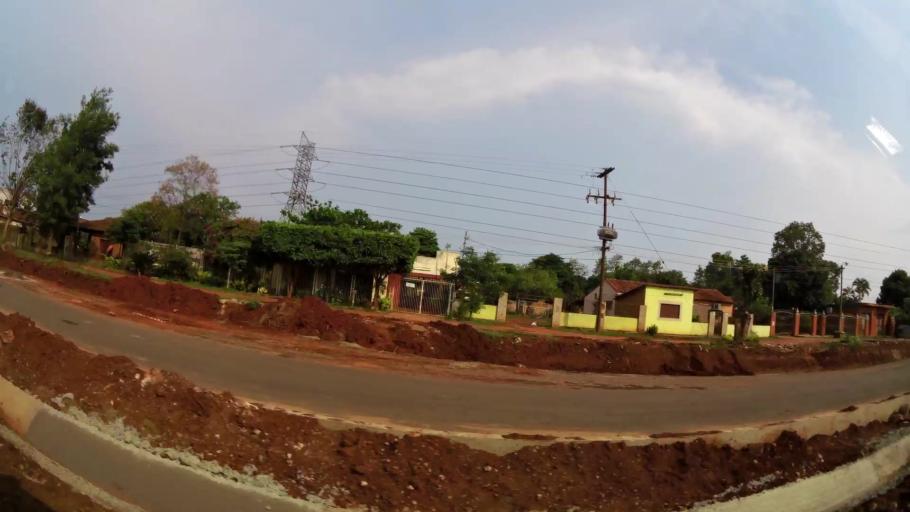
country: PY
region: Alto Parana
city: Ciudad del Este
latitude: -25.4717
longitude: -54.6459
